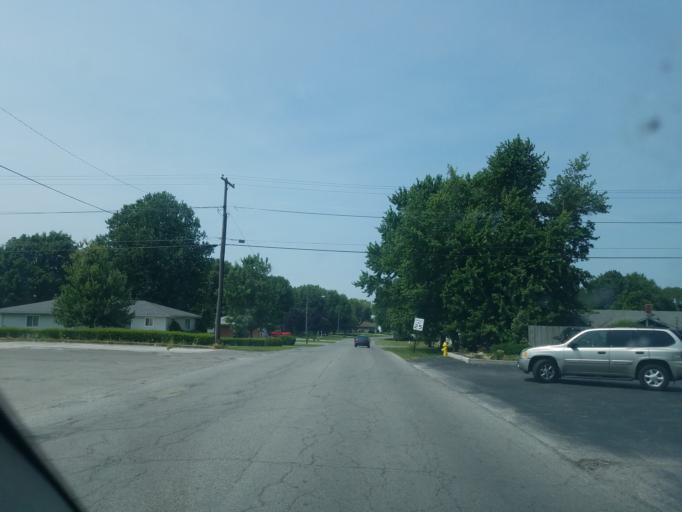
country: US
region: Ohio
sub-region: Seneca County
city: Tiffin
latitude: 41.1136
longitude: -83.2068
